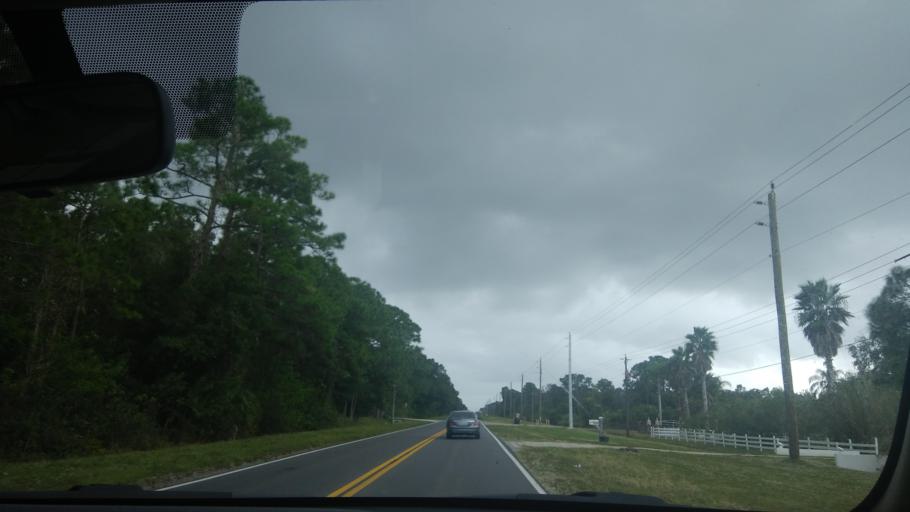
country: US
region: Florida
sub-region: Brevard County
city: Grant-Valkaria
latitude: 27.9742
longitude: -80.6225
